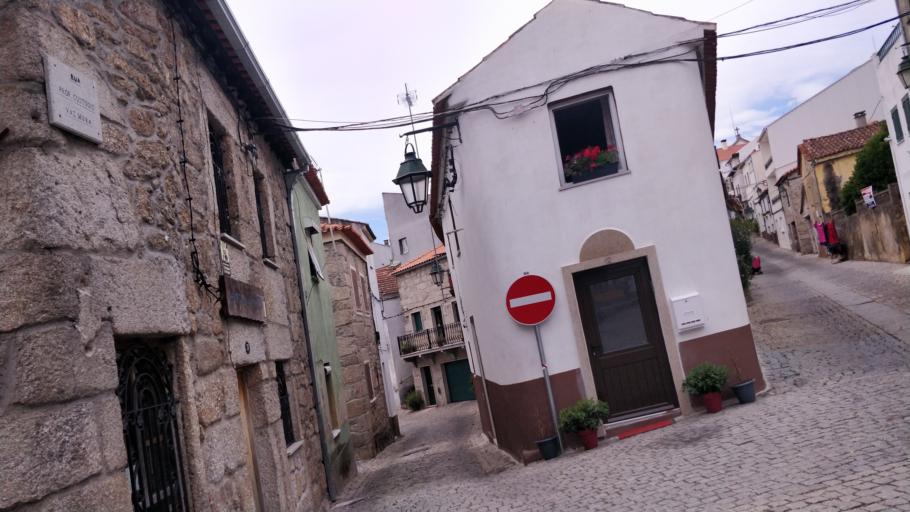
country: PT
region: Castelo Branco
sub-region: Belmonte
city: Belmonte
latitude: 40.3586
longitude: -7.3491
